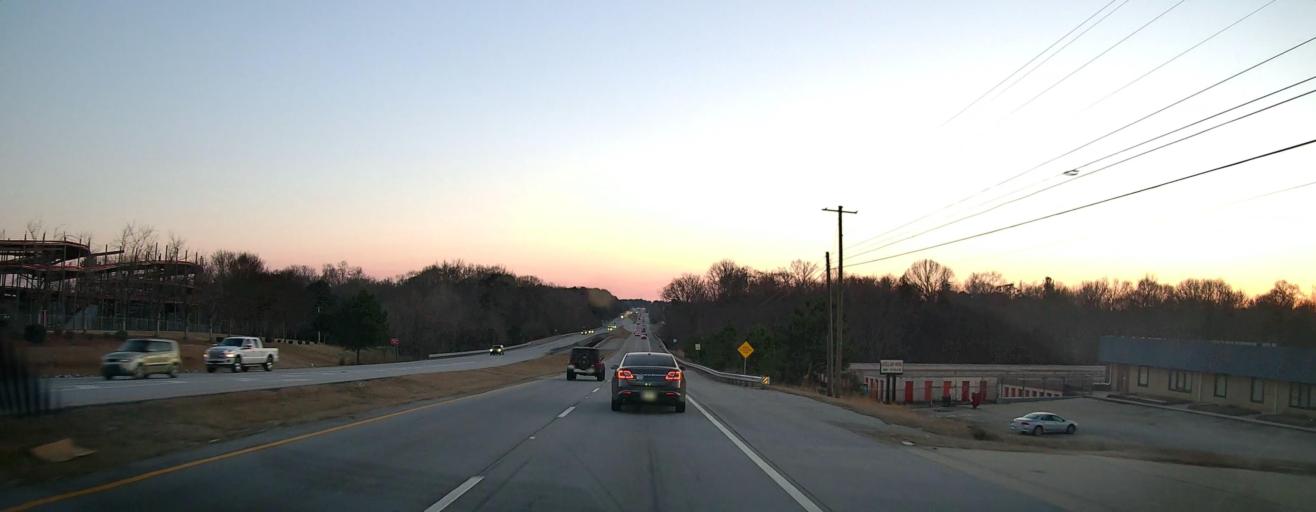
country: US
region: Georgia
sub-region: Fayette County
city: Fayetteville
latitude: 33.4970
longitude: -84.4293
